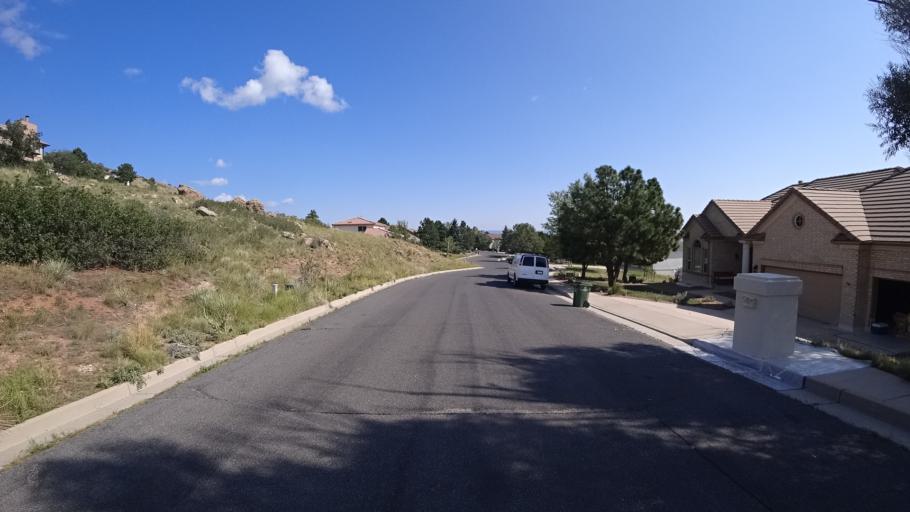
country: US
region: Colorado
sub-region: El Paso County
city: Manitou Springs
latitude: 38.9083
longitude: -104.8772
